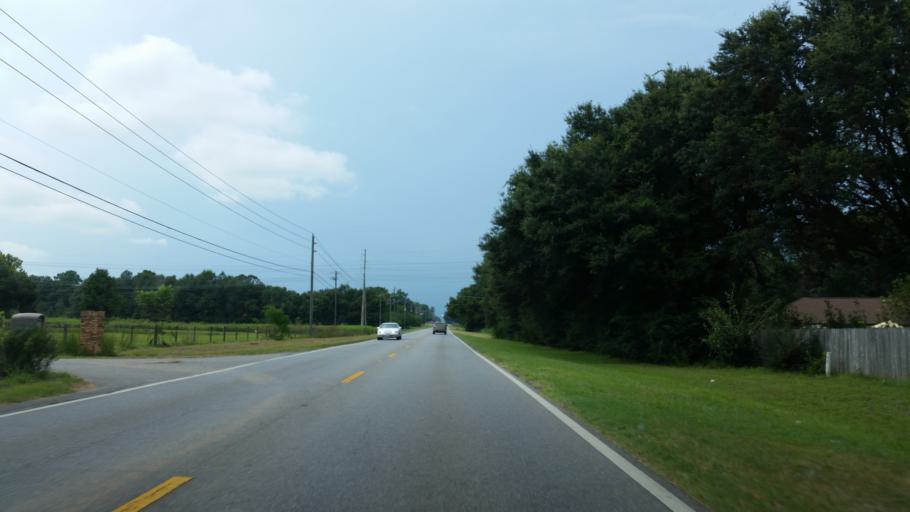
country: US
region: Florida
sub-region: Santa Rosa County
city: Wallace
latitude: 30.6384
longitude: -87.1762
